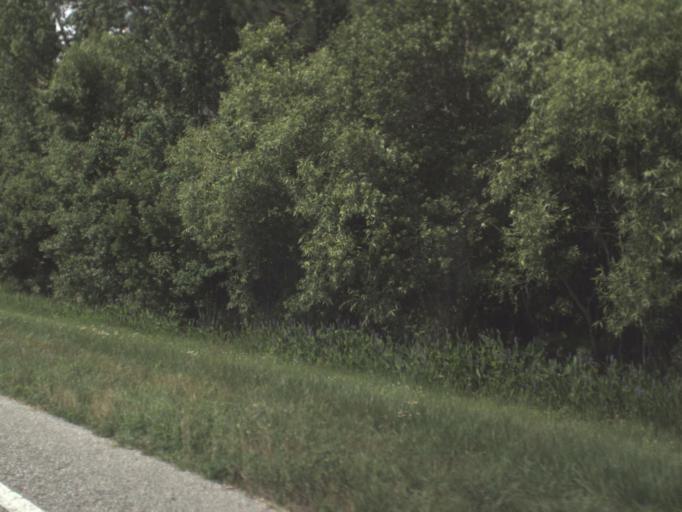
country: US
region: Florida
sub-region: Saint Johns County
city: Saint Augustine Shores
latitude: 29.7413
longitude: -81.3092
